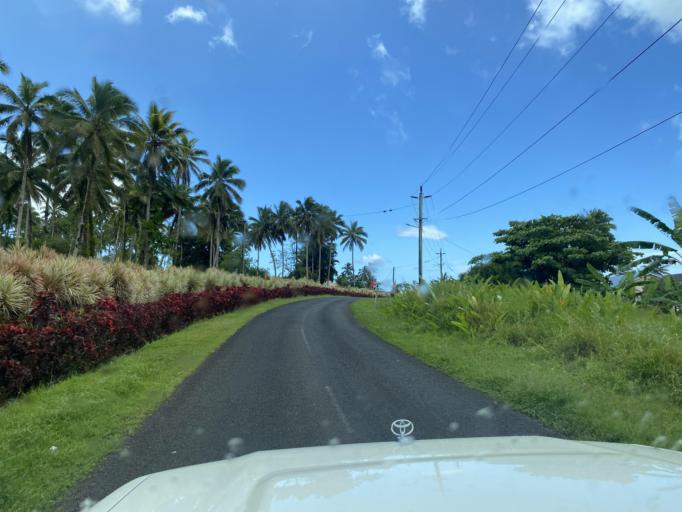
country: WS
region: Va`a-o-Fonoti
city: Samamea
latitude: -13.9829
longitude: -171.5876
